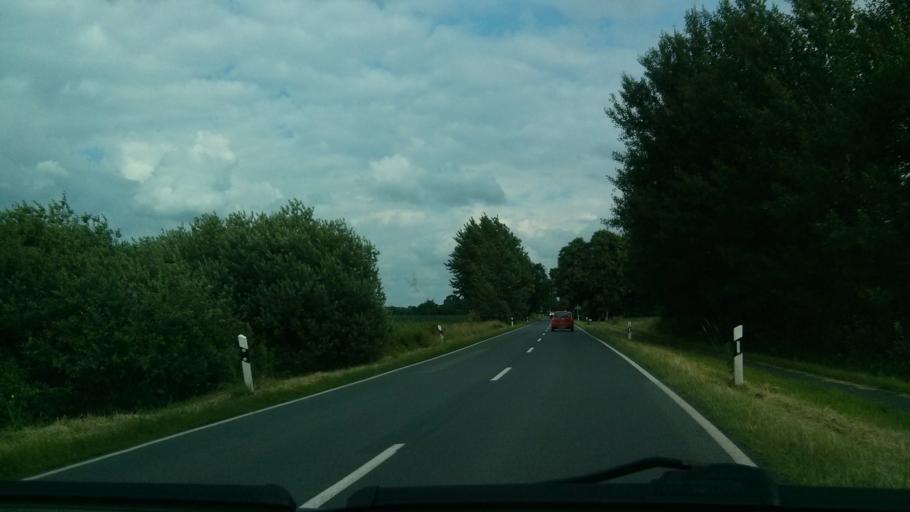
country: DE
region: Lower Saxony
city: Kuhrstedt
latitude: 53.5103
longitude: 8.7702
